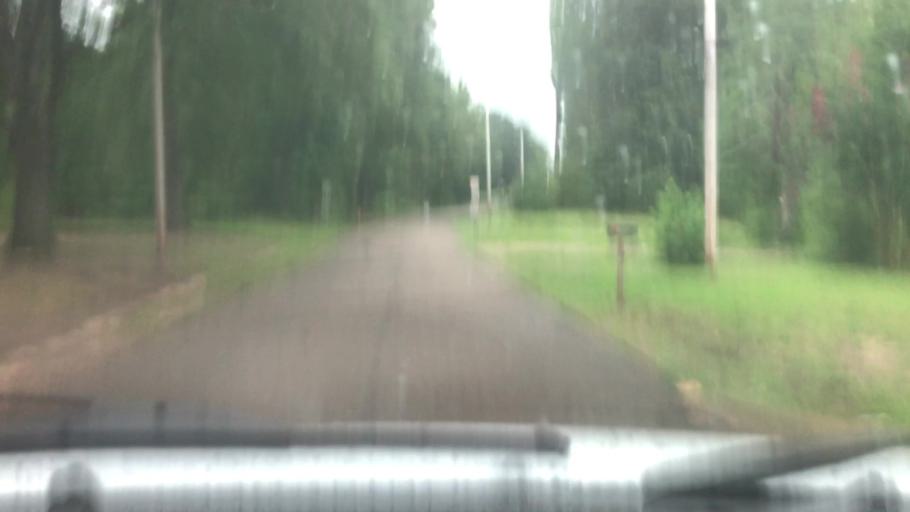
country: US
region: Texas
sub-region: Bowie County
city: Wake Village
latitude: 33.3958
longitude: -94.0858
